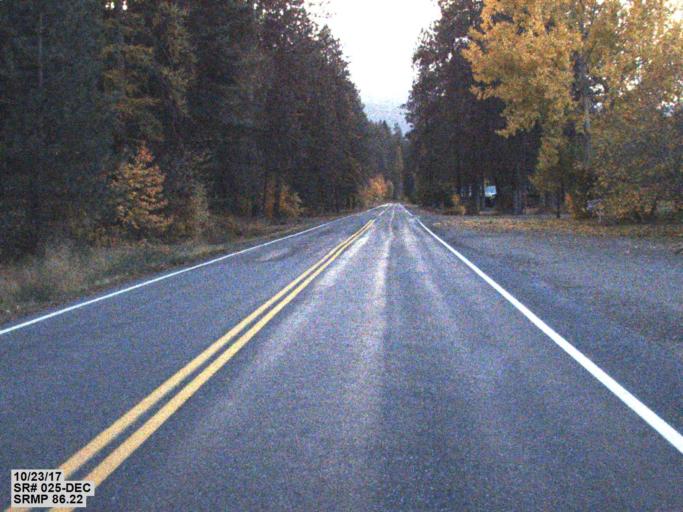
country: US
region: Washington
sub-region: Stevens County
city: Kettle Falls
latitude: 48.6637
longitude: -118.0617
